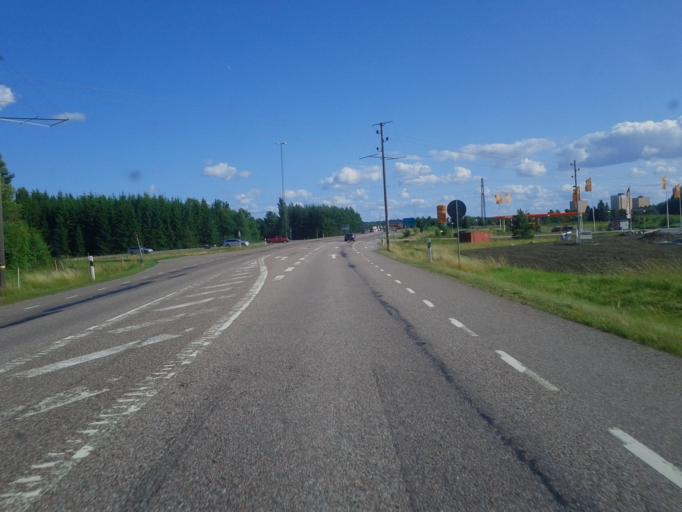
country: SE
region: Uppsala
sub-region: Enkopings Kommun
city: Enkoping
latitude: 59.6595
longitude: 17.0770
